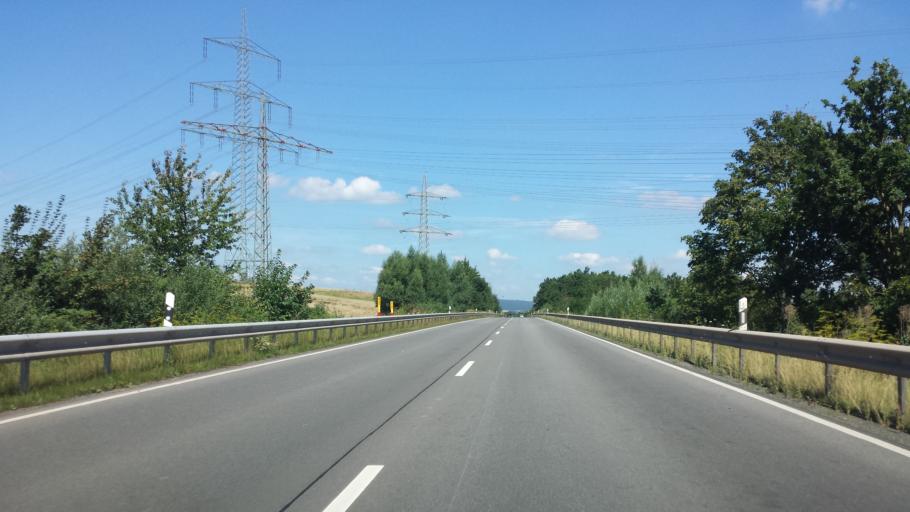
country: DE
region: Rheinland-Pfalz
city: Gollheim
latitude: 49.5839
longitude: 8.0452
